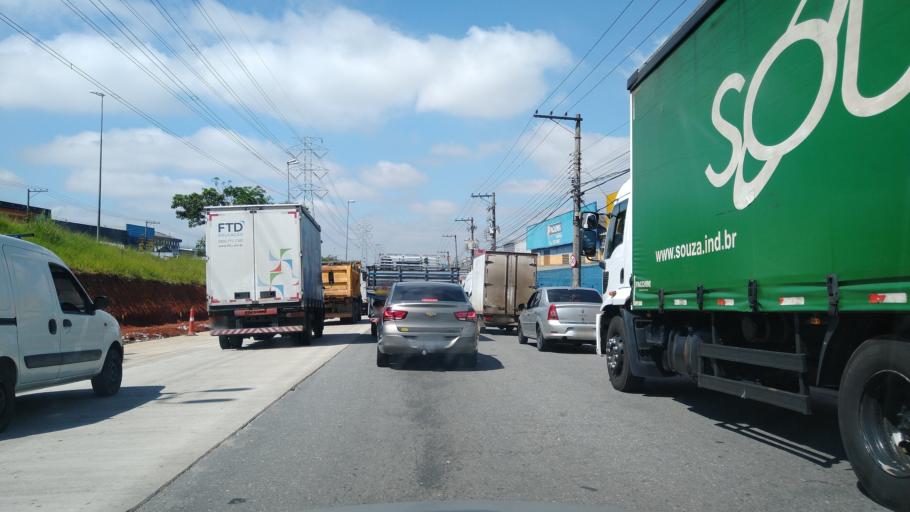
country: BR
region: Sao Paulo
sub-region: Guarulhos
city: Guarulhos
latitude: -23.4606
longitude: -46.4707
